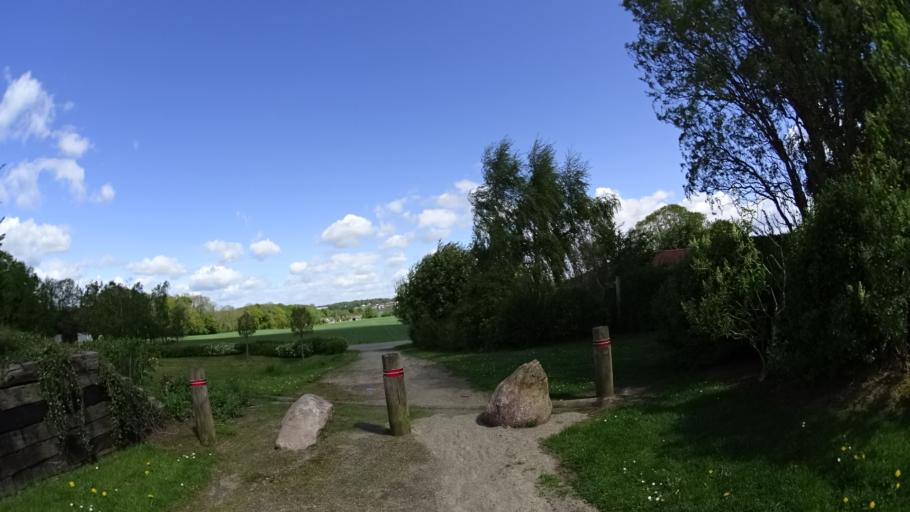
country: DK
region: Central Jutland
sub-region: Arhus Kommune
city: Stavtrup
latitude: 56.1328
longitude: 10.1086
